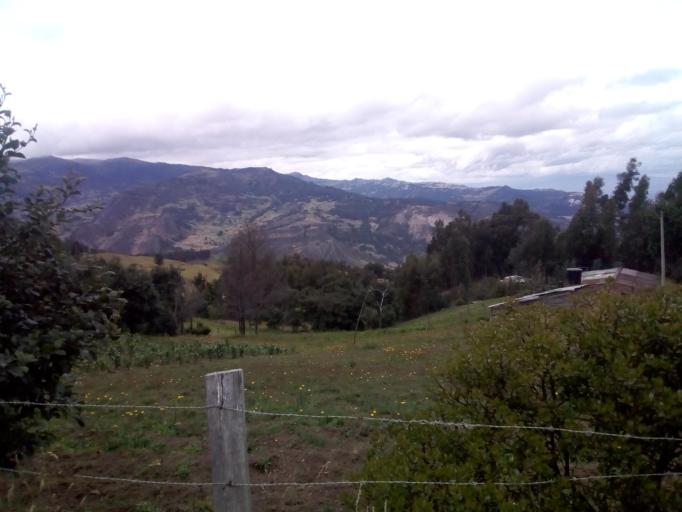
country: CO
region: Boyaca
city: Gameza
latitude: 5.8152
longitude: -72.7945
